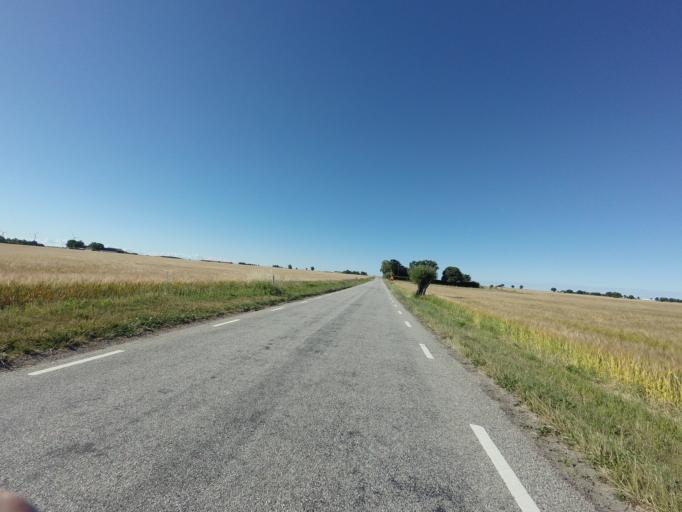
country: SE
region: Skane
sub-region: Trelleborgs Kommun
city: Skare
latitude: 55.4021
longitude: 13.0195
